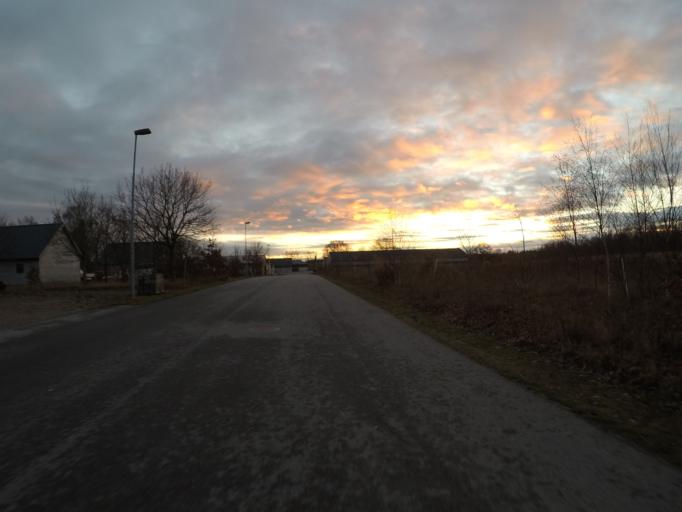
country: SE
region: Skane
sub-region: Sjobo Kommun
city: Sjoebo
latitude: 55.6454
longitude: 13.6930
